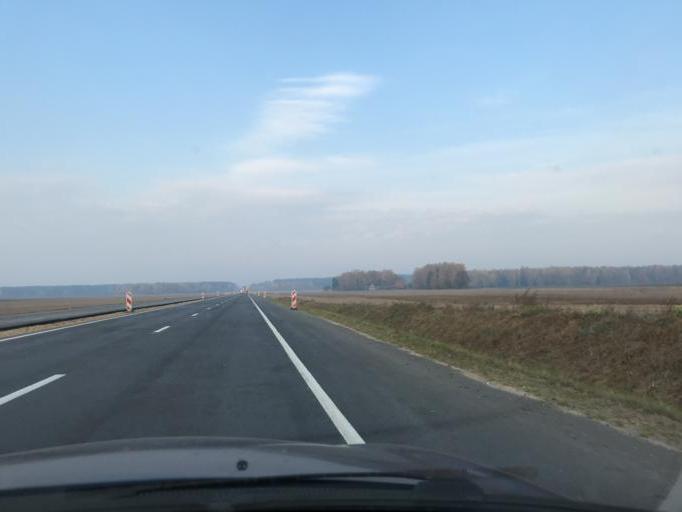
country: BY
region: Grodnenskaya
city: Lida
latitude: 53.8407
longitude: 25.2626
